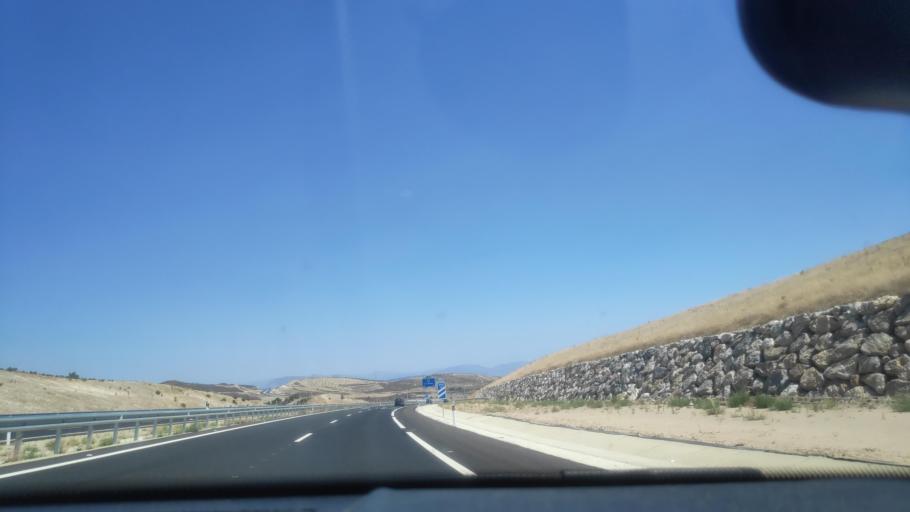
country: ES
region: Andalusia
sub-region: Provincia de Granada
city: Alhendin
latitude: 37.0952
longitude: -3.6736
